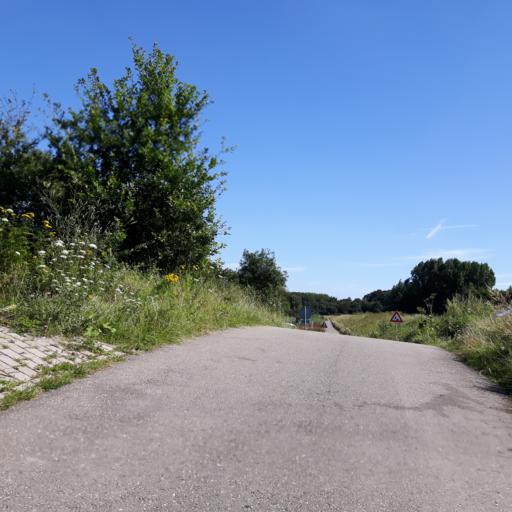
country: NL
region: North Brabant
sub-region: Gemeente Bergen op Zoom
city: Bergen op Zoom
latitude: 51.4720
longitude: 4.2878
